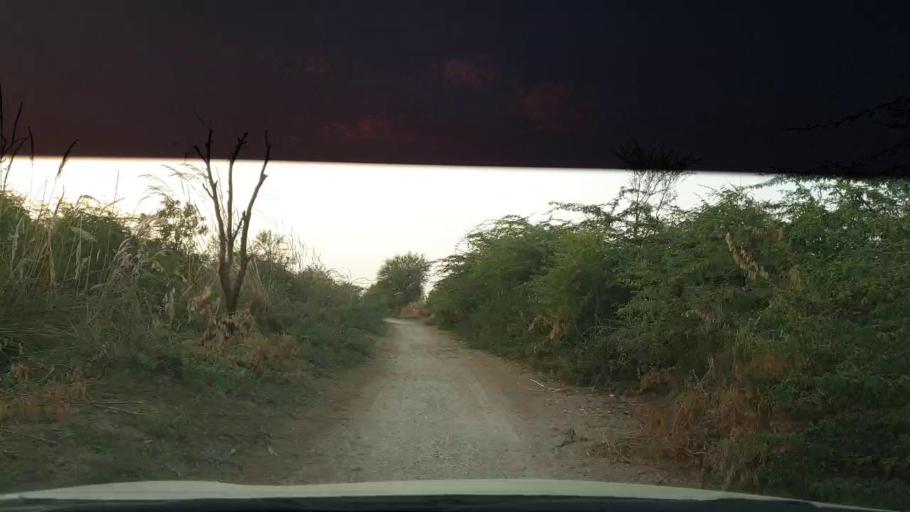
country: PK
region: Sindh
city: Berani
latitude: 25.7616
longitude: 68.9897
